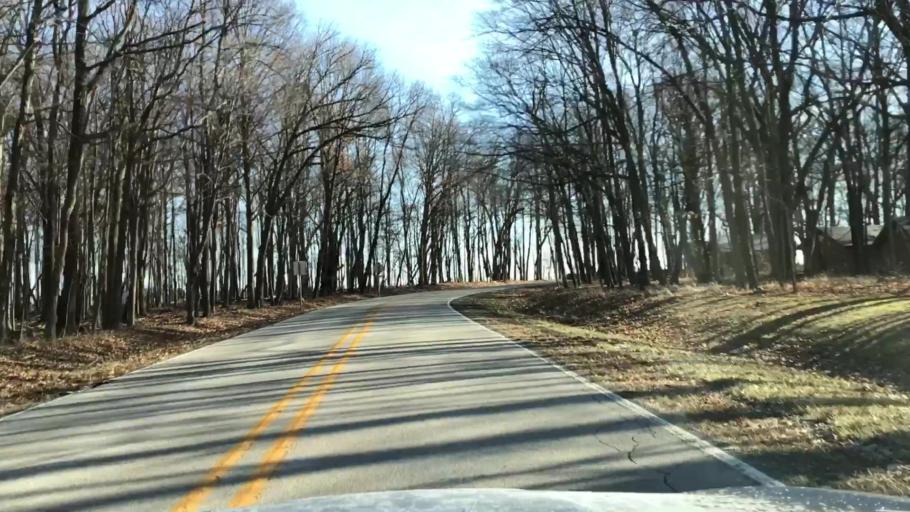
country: US
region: Illinois
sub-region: McLean County
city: Hudson
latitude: 40.6486
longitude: -88.9107
